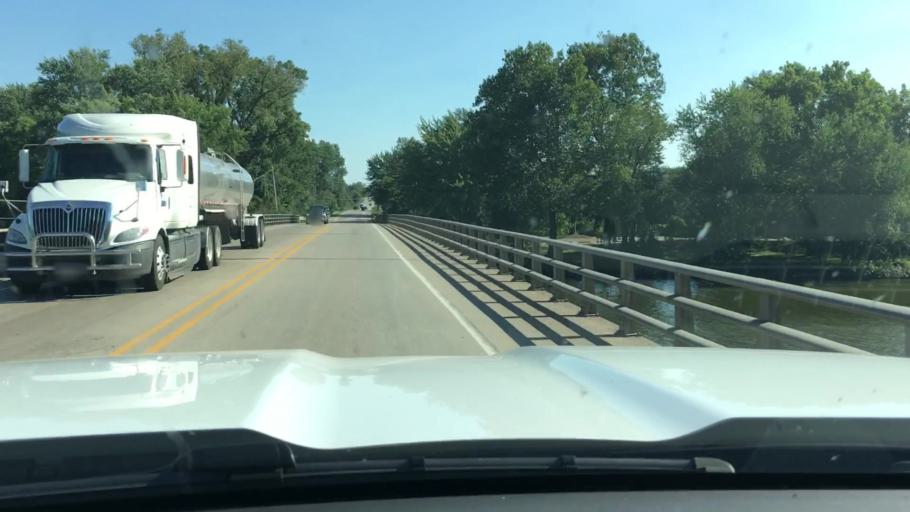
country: US
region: Michigan
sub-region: Ottawa County
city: Allendale
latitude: 43.0156
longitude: -85.9557
